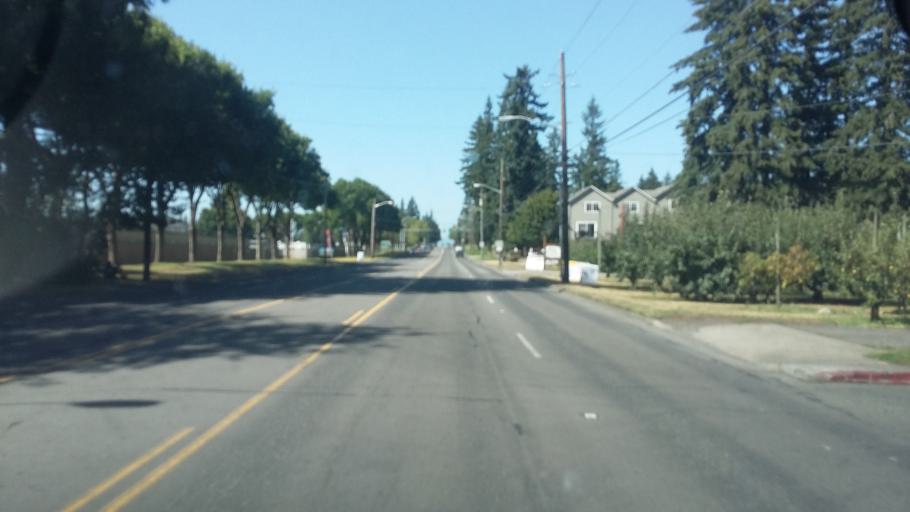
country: US
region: Washington
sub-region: Clark County
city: Orchards
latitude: 45.6257
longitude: -122.5576
